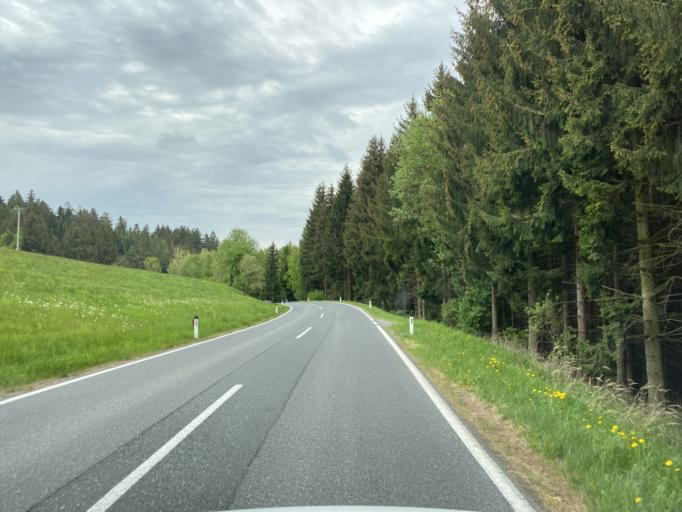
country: AT
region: Styria
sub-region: Politischer Bezirk Weiz
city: Gschaid bei Birkfeld
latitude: 47.3453
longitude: 15.7398
